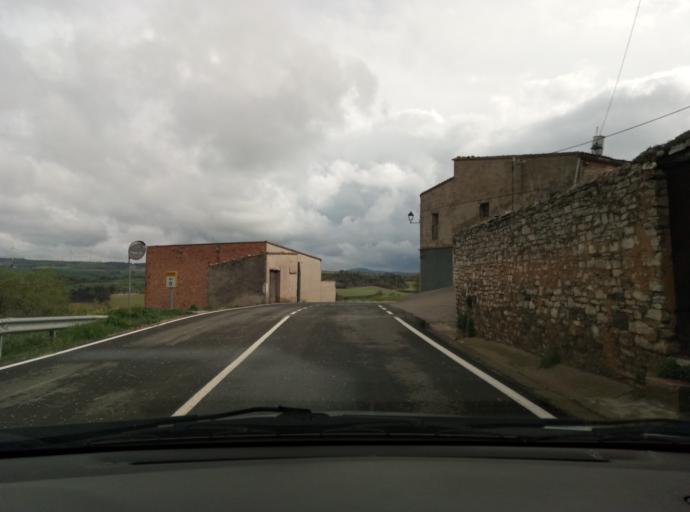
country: ES
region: Catalonia
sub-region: Provincia de Tarragona
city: Santa Coloma de Queralt
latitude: 41.5819
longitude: 1.3390
